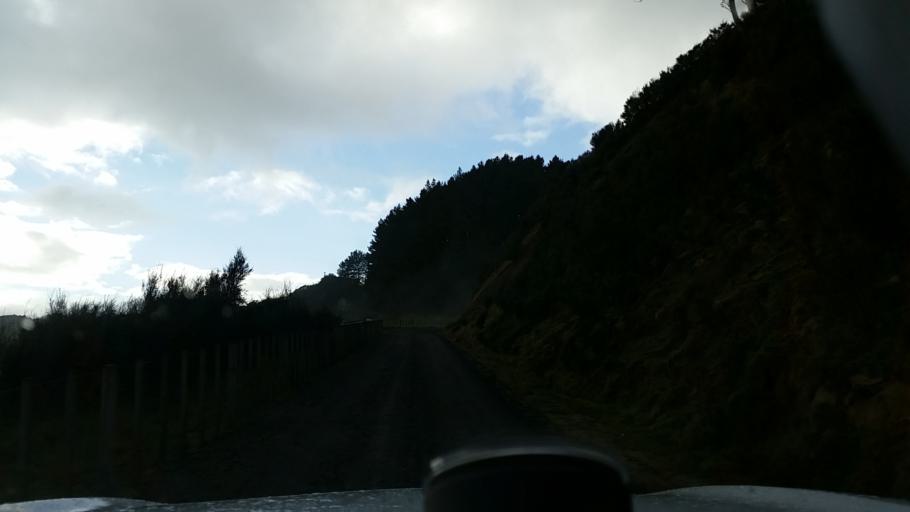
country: NZ
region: Taranaki
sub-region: South Taranaki District
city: Eltham
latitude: -39.4082
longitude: 174.5404
